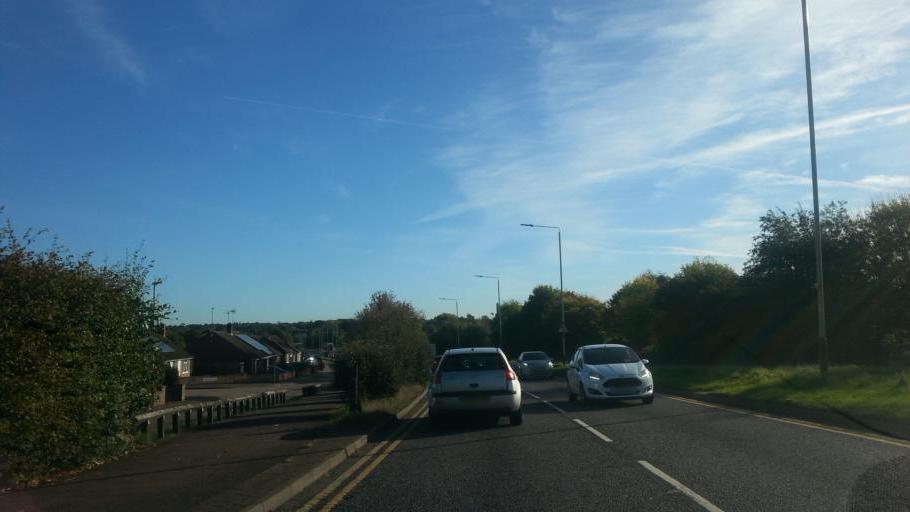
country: GB
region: England
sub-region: Leicestershire
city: Wigston Magna
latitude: 52.5973
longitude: -1.1249
